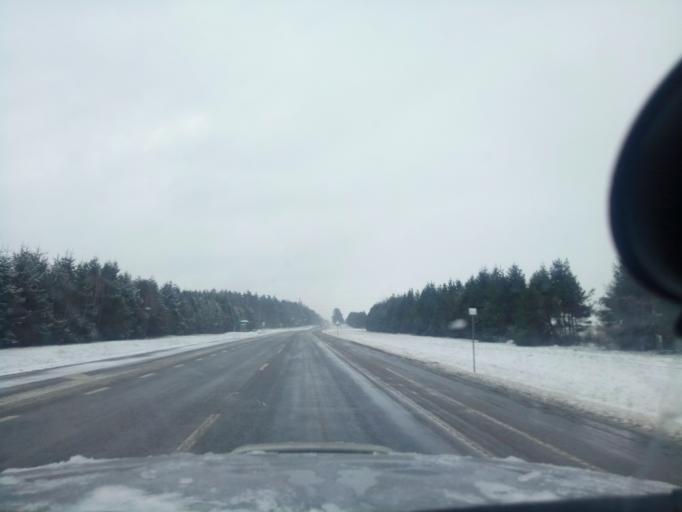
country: BY
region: Minsk
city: Haradzyeya
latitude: 53.2867
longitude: 26.5835
